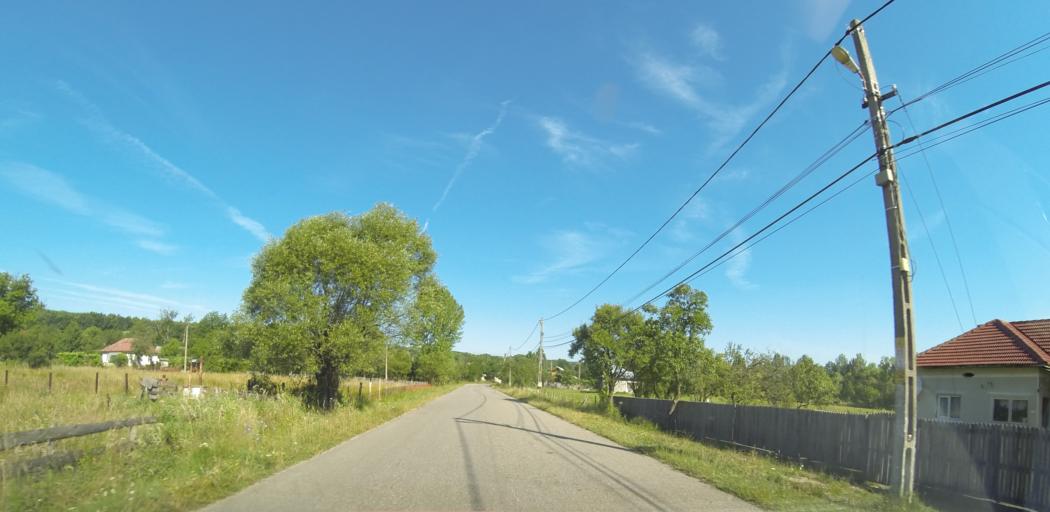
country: RO
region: Valcea
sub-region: Comuna Slatioara
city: Slatioara
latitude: 45.1340
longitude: 23.8763
